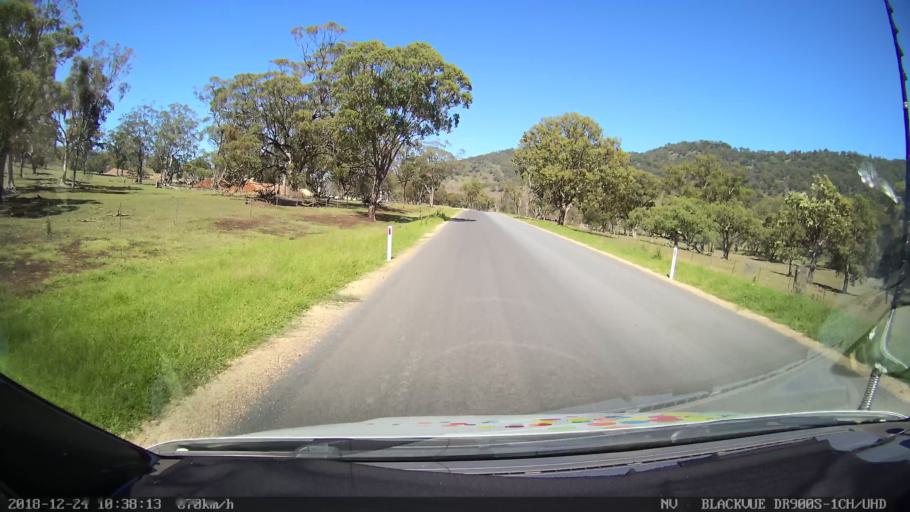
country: AU
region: New South Wales
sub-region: Upper Hunter Shire
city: Merriwa
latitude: -31.8480
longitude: 150.4843
